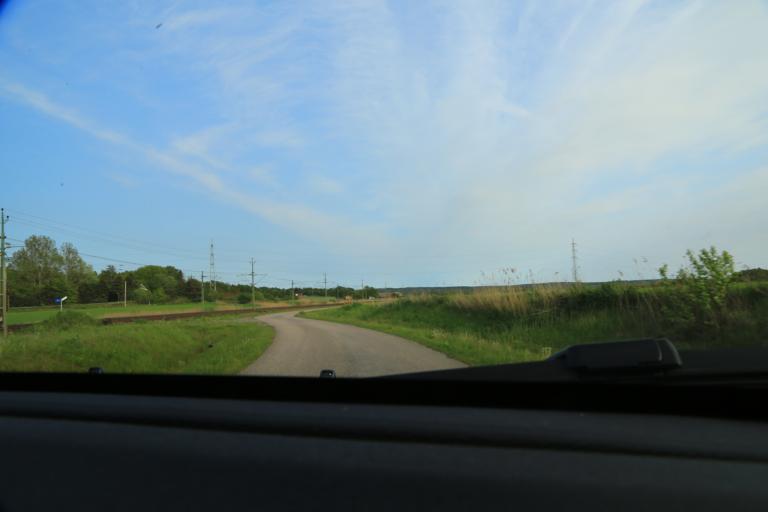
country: SE
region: Halland
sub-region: Kungsbacka Kommun
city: Frillesas
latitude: 57.2384
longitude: 12.1957
